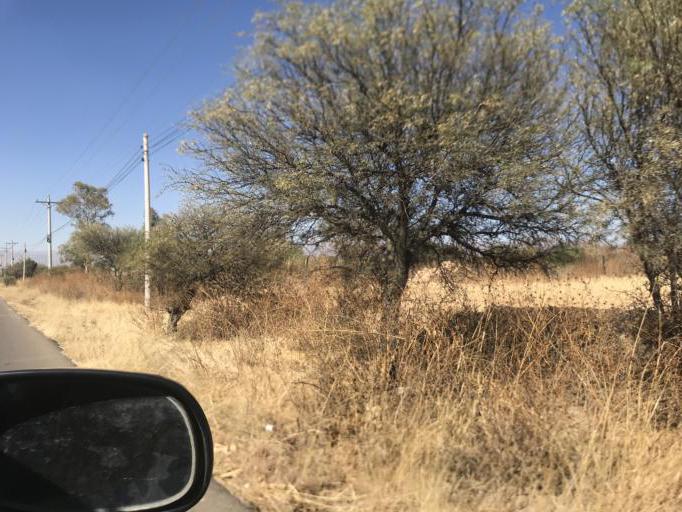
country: BO
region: Cochabamba
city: Cliza
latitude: -17.5998
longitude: -65.9652
